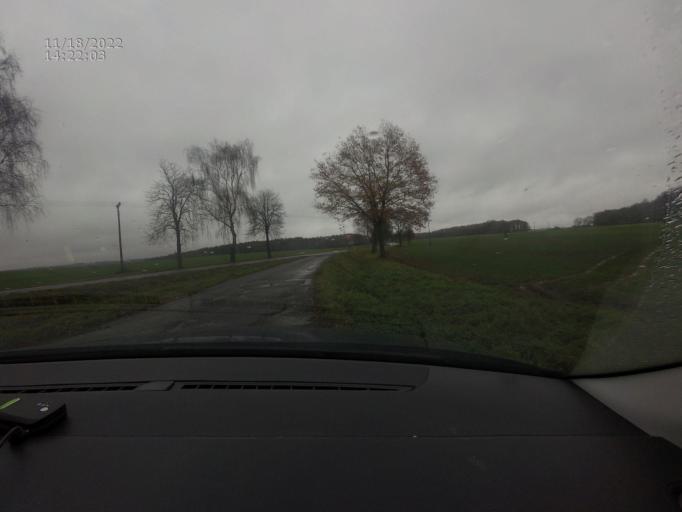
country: CZ
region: Jihocesky
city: Cimelice
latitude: 49.4401
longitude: 14.1003
